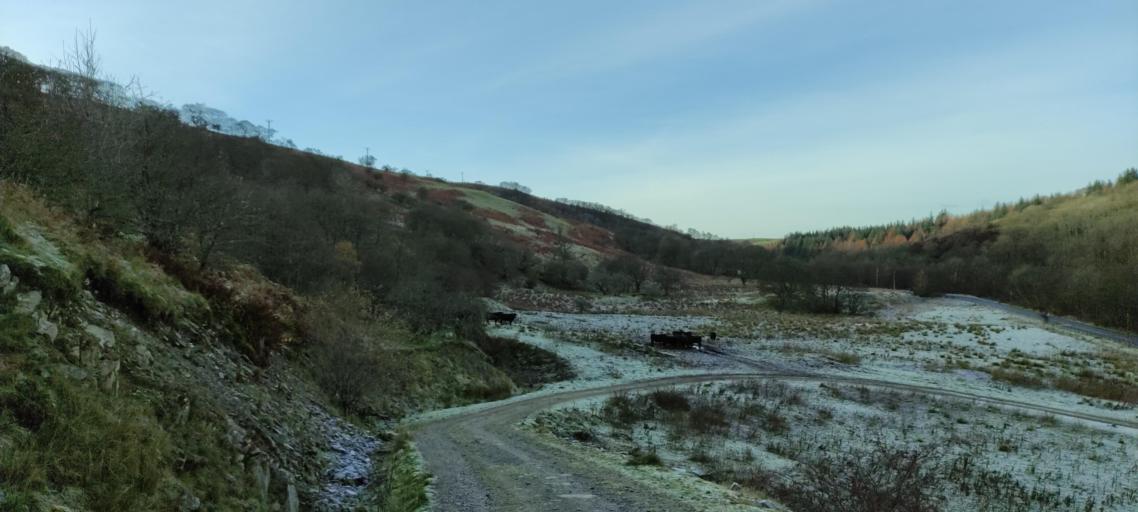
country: GB
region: Scotland
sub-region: Dumfries and Galloway
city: Langholm
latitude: 55.1426
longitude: -3.0172
